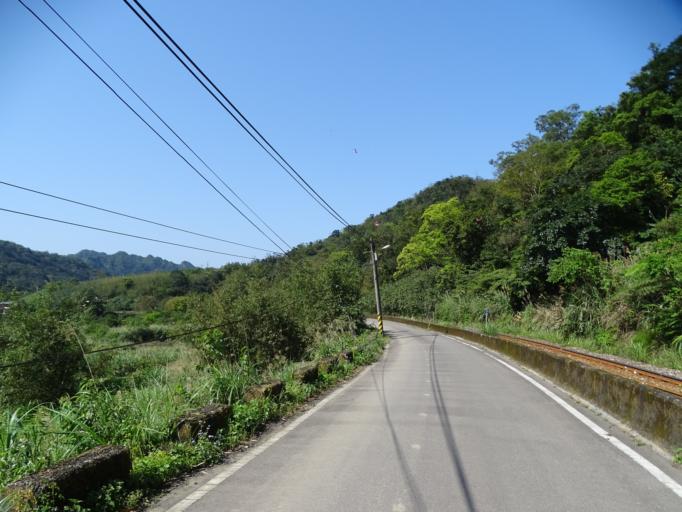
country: TW
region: Taiwan
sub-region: Keelung
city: Keelung
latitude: 25.0393
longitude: 121.7706
